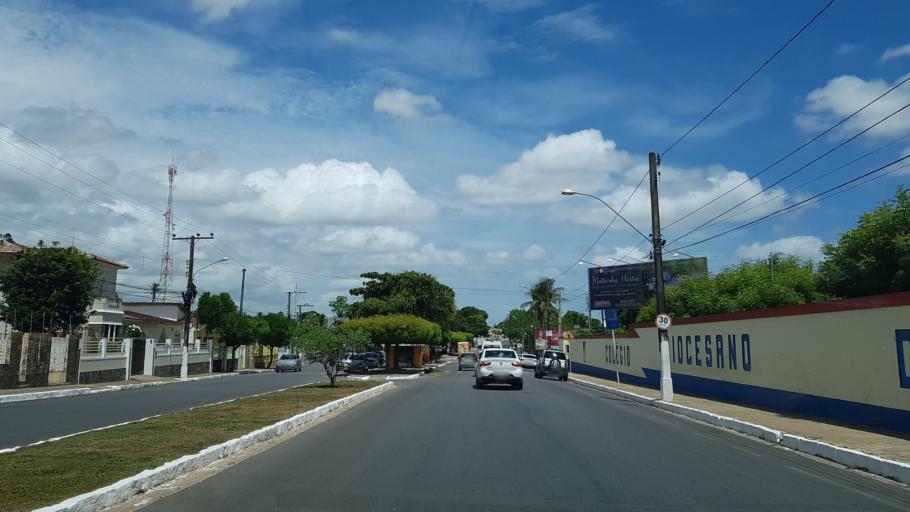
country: BR
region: Alagoas
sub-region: Penedo
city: Penedo
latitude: -10.2836
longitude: -36.5712
